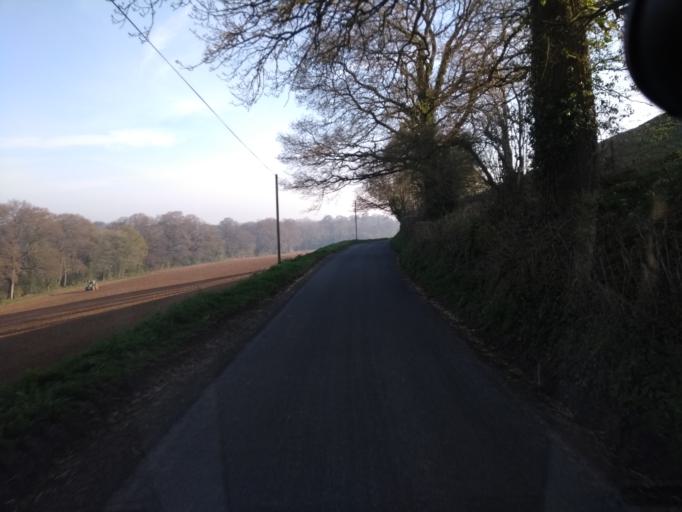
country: GB
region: England
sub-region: Somerset
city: Crewkerne
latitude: 50.8938
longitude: -2.8273
